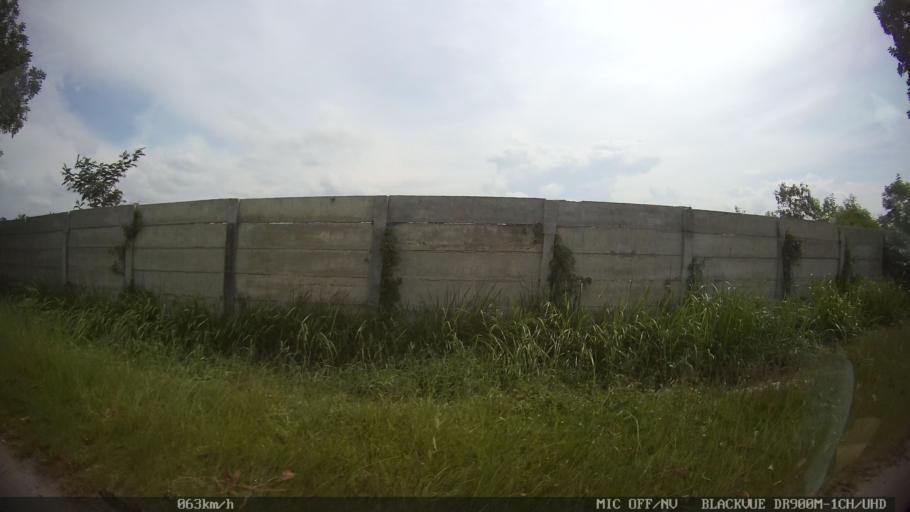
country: ID
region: North Sumatra
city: Percut
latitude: 3.6143
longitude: 98.8421
